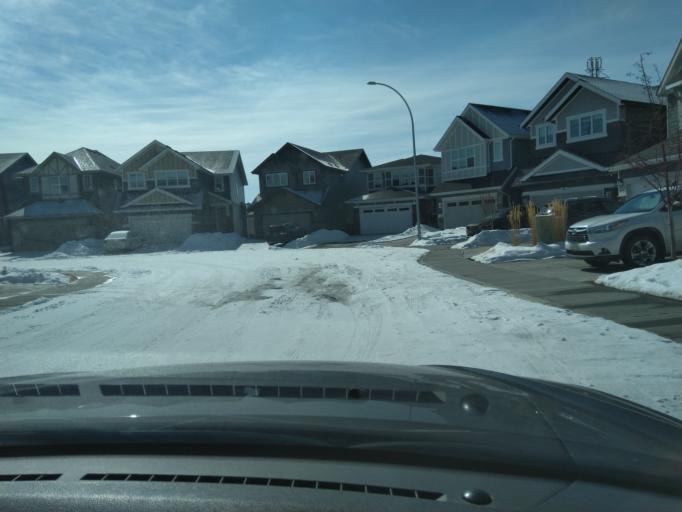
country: CA
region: Alberta
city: Calgary
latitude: 51.1309
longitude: -114.2561
